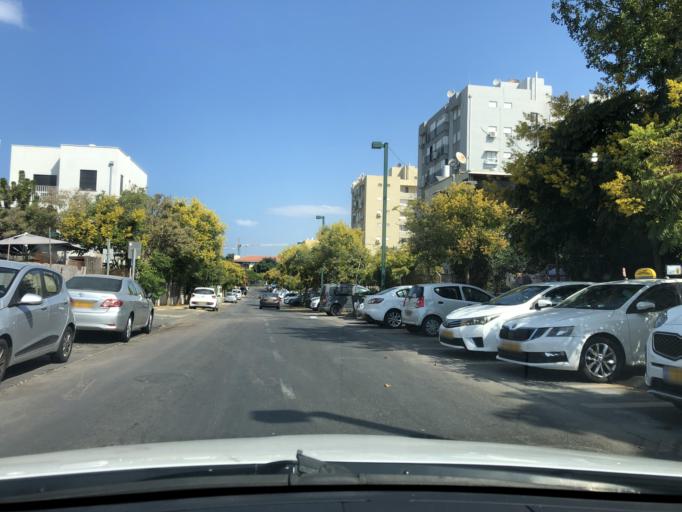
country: IL
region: Tel Aviv
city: Yafo
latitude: 32.0416
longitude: 34.7561
